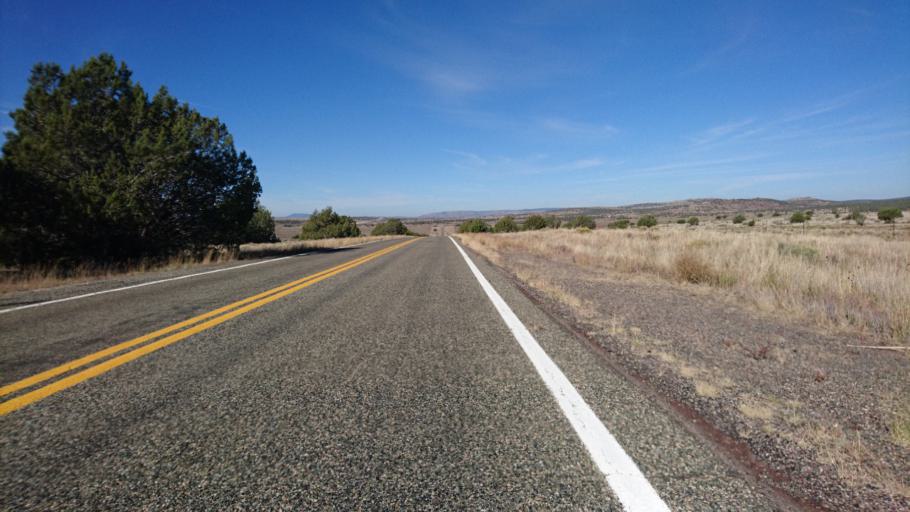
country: US
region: Arizona
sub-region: Yavapai County
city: Paulden
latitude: 35.2820
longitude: -112.7107
